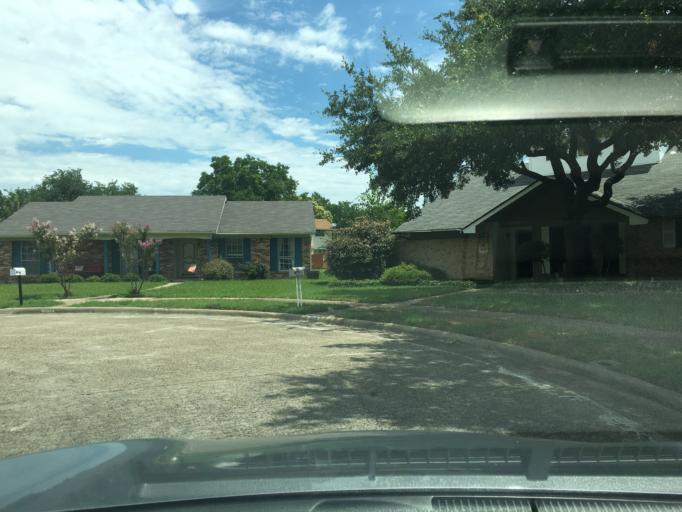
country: US
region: Texas
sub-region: Dallas County
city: Richardson
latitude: 32.9337
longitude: -96.6854
